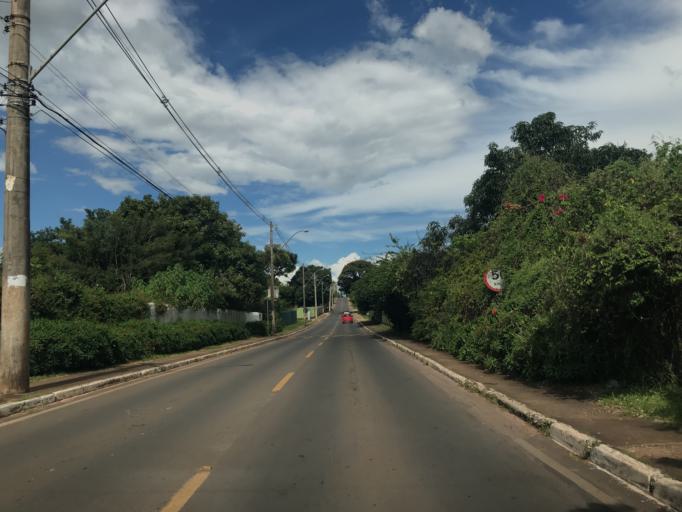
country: BR
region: Federal District
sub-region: Brasilia
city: Brasilia
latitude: -15.7185
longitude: -47.8775
